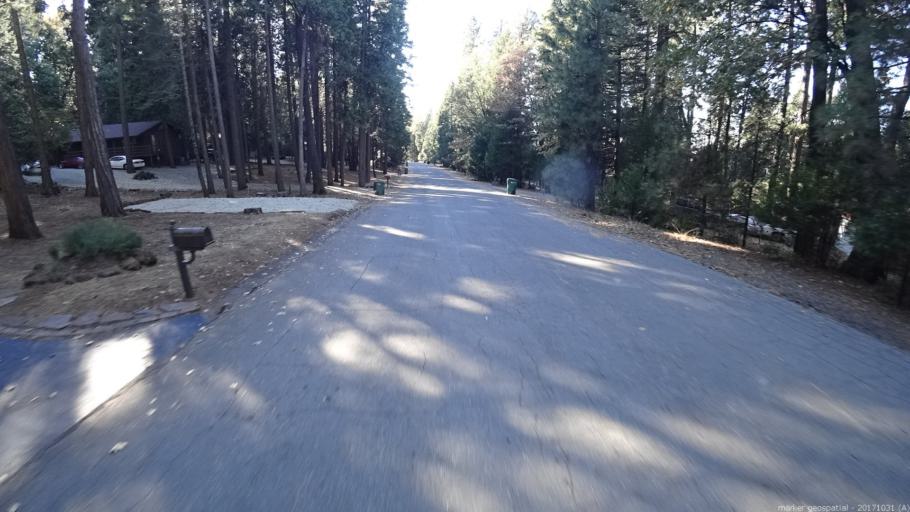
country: US
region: California
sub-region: Shasta County
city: Shingletown
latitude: 40.5045
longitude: -121.9080
